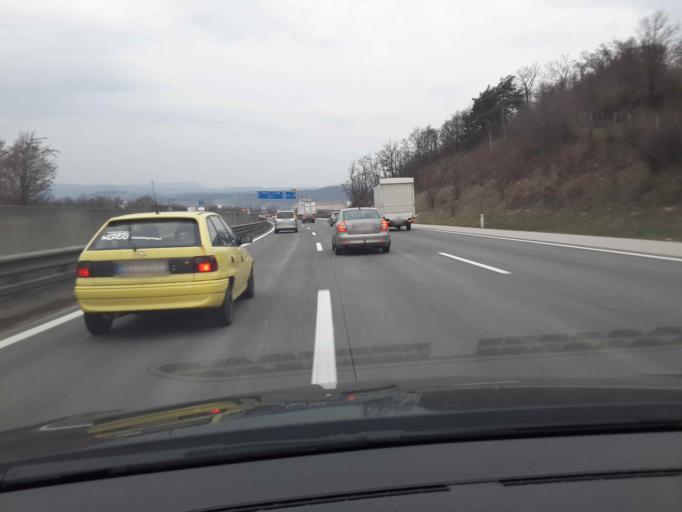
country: AT
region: Lower Austria
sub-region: Politischer Bezirk Melk
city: Melk
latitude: 48.2142
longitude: 15.3572
